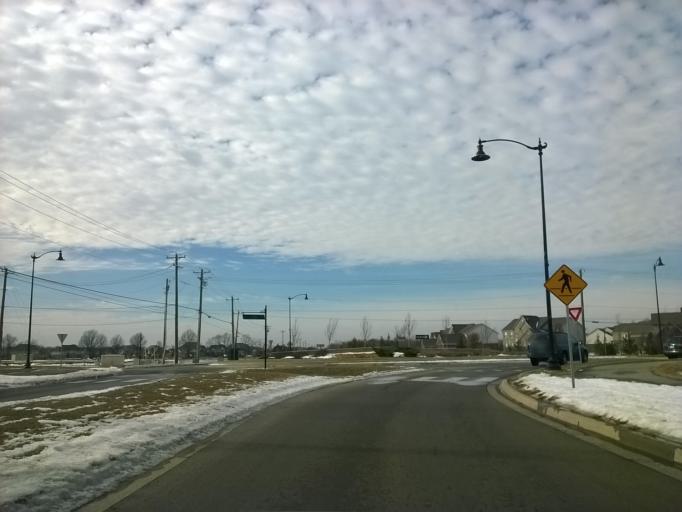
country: US
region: Indiana
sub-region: Boone County
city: Zionsville
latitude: 39.9774
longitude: -86.2208
